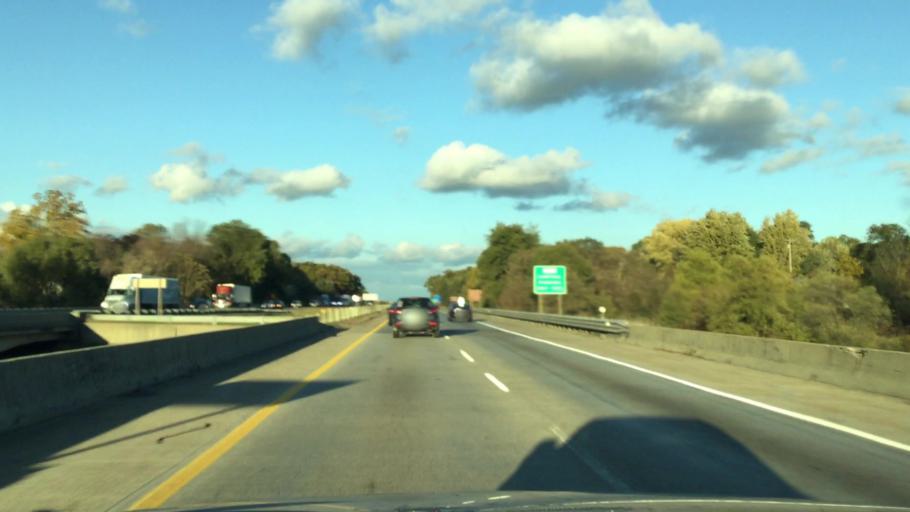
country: US
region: Michigan
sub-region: Calhoun County
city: Battle Creek
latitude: 42.2734
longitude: -85.1693
